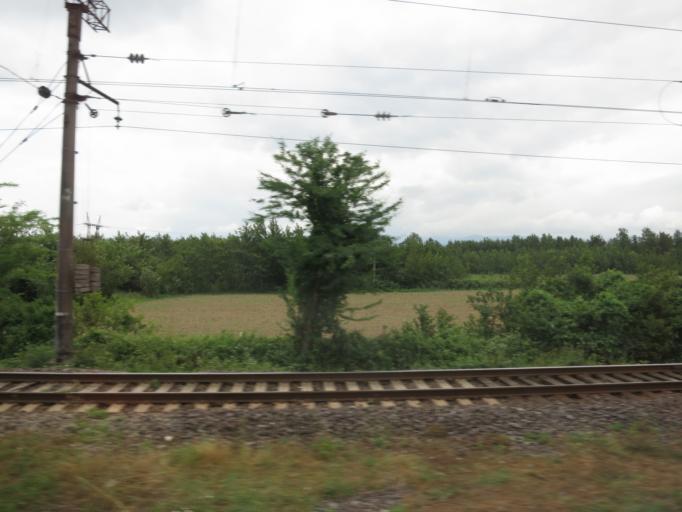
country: GE
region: Imereti
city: K'ulashi
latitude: 42.1767
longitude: 42.4132
